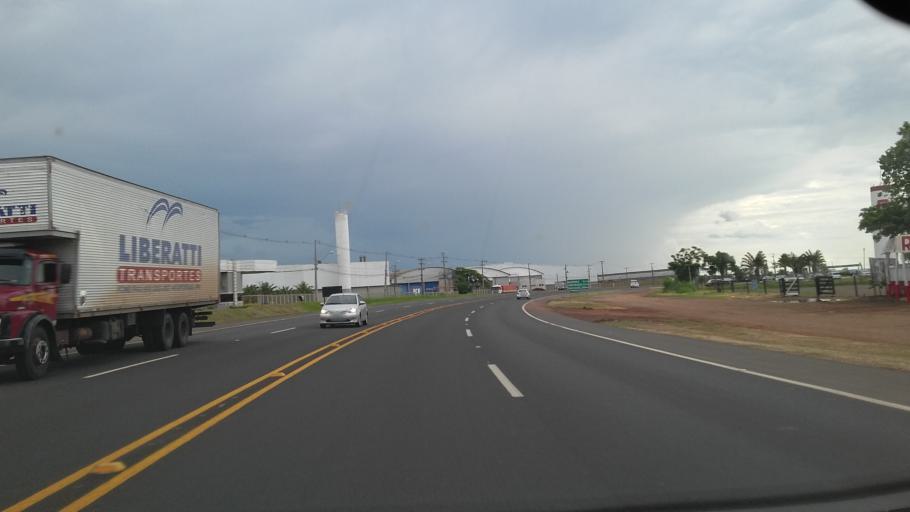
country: BR
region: Parana
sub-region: Arapongas
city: Arapongas
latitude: -23.4083
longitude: -51.4674
